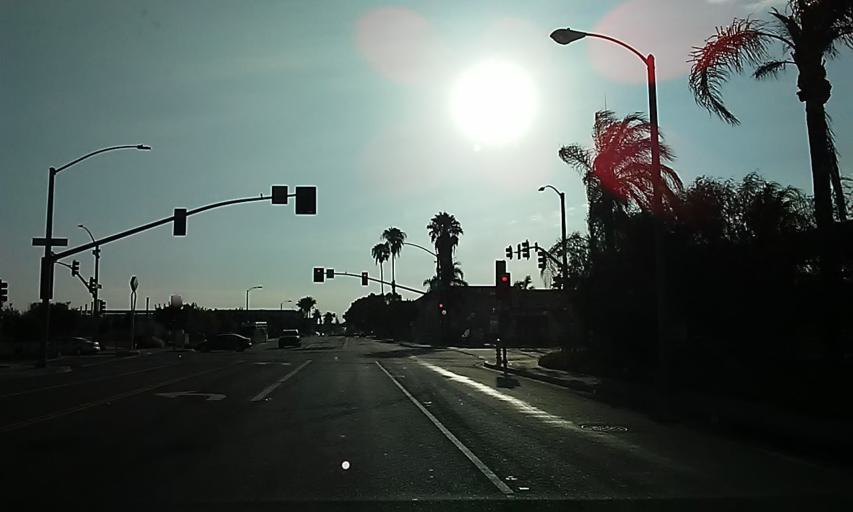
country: US
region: California
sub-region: San Bernardino County
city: San Bernardino
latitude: 34.1009
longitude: -117.2936
